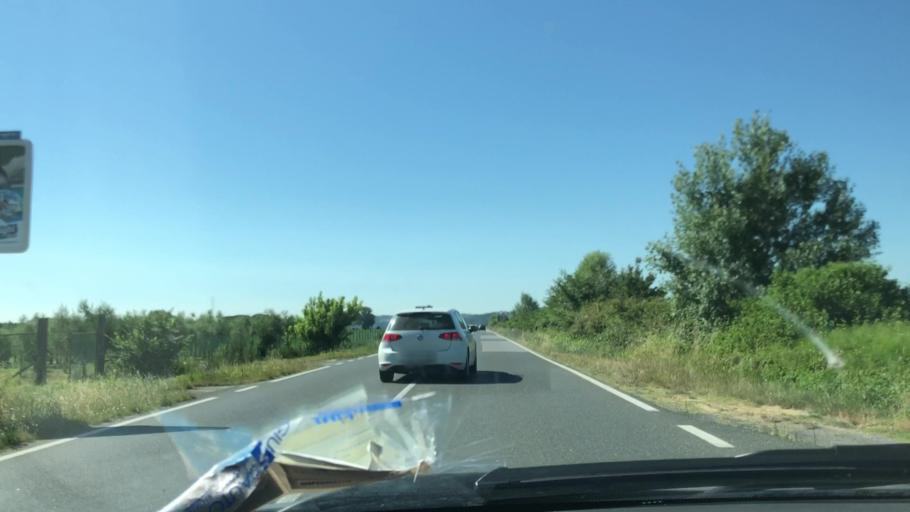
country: IT
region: Tuscany
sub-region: Province of Pisa
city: Forcoli
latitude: 43.5958
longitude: 10.6978
